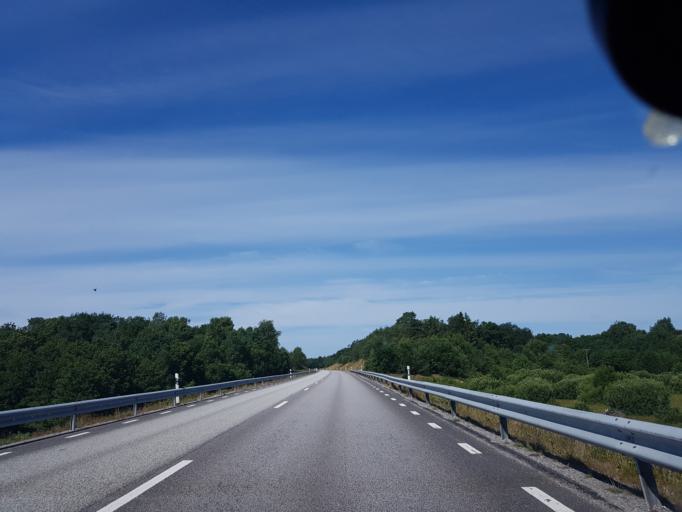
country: SE
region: Vaestra Goetaland
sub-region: Orust
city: Henan
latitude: 58.1549
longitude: 11.5578
